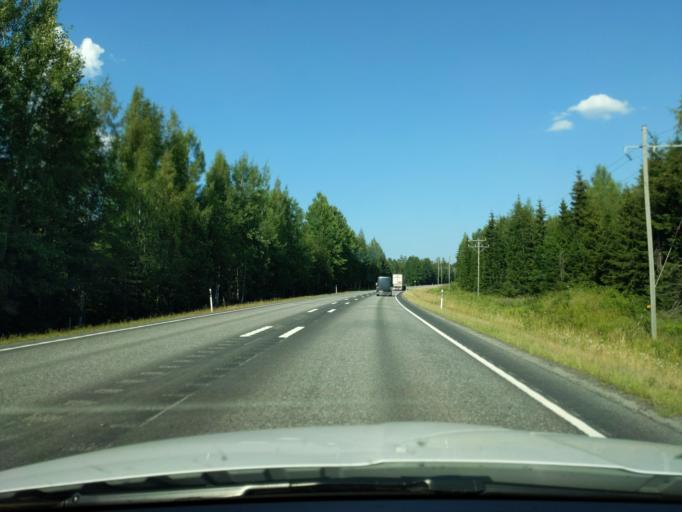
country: FI
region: Paijanne Tavastia
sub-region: Lahti
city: Hollola
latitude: 60.9359
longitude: 25.3891
